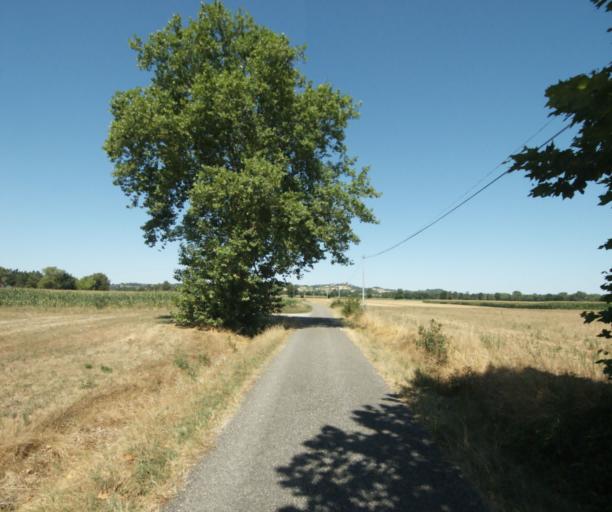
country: FR
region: Midi-Pyrenees
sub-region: Departement de la Haute-Garonne
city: Revel
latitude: 43.4855
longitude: 1.9657
